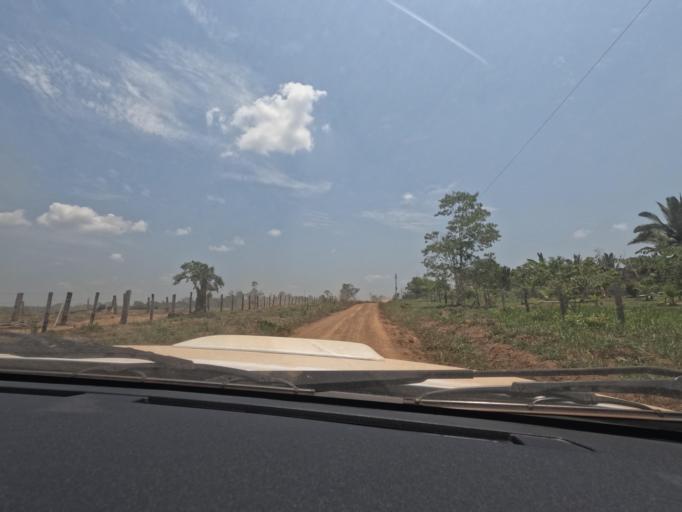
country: BR
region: Rondonia
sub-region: Porto Velho
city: Porto Velho
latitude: -8.6508
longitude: -64.1687
